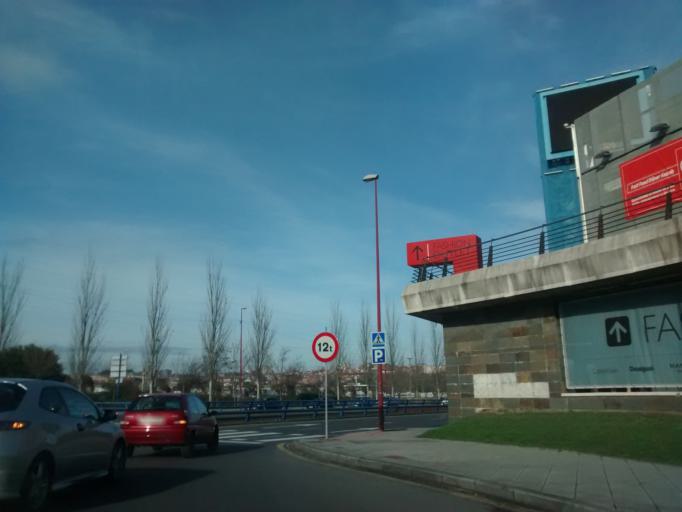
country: ES
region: Basque Country
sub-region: Bizkaia
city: Barakaldo
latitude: 43.2936
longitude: -3.0054
